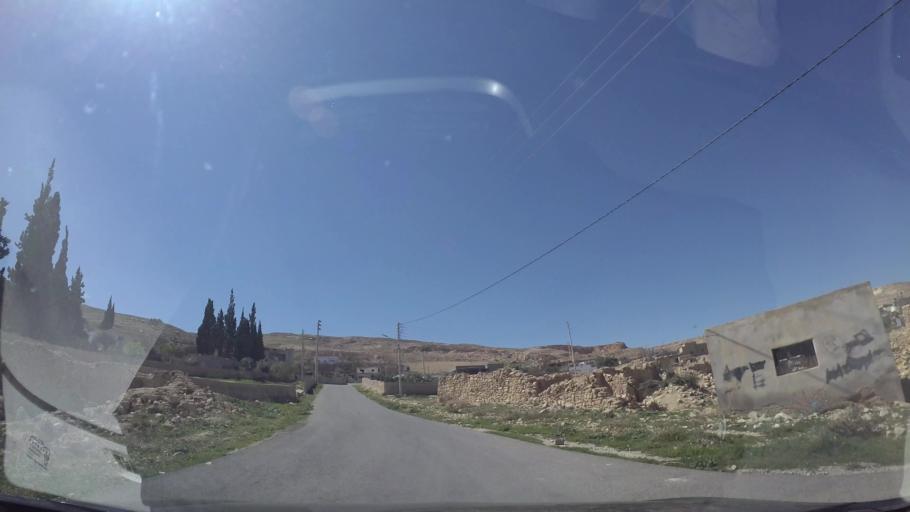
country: JO
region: Tafielah
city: At Tafilah
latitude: 30.8413
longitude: 35.5670
